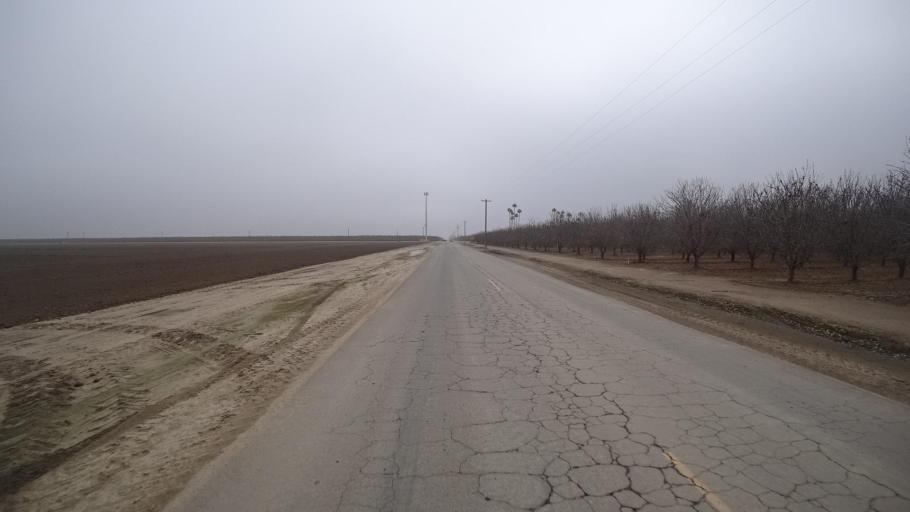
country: US
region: California
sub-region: Kern County
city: Greenfield
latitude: 35.2380
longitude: -119.0602
